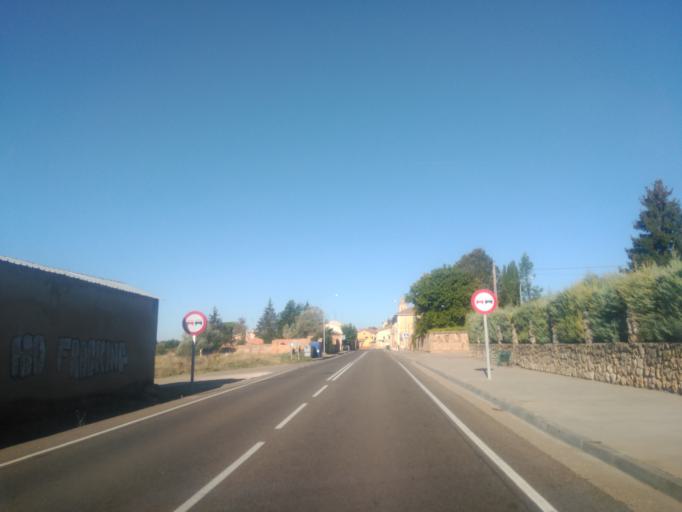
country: ES
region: Castille and Leon
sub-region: Provincia de Burgos
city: Zazuar
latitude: 41.6945
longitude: -3.5503
